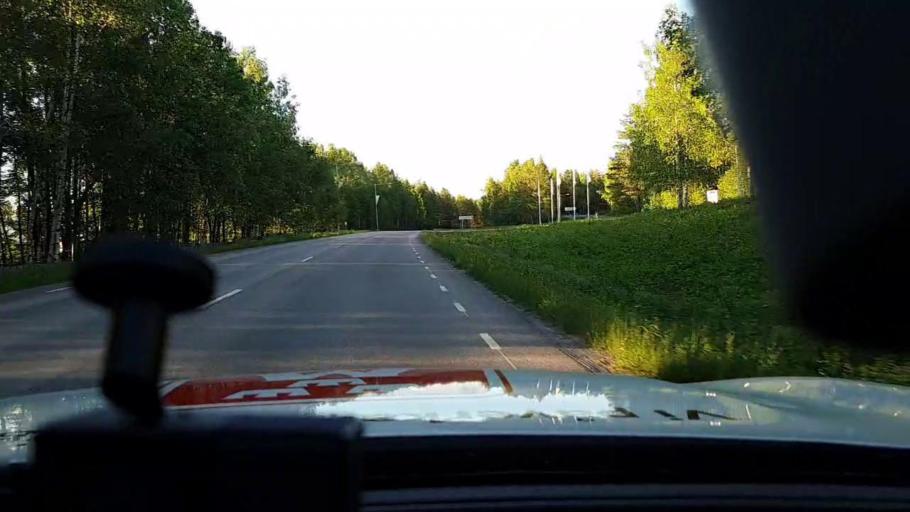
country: SE
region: Norrbotten
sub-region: Lulea Kommun
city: Lulea
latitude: 65.6107
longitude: 22.1890
